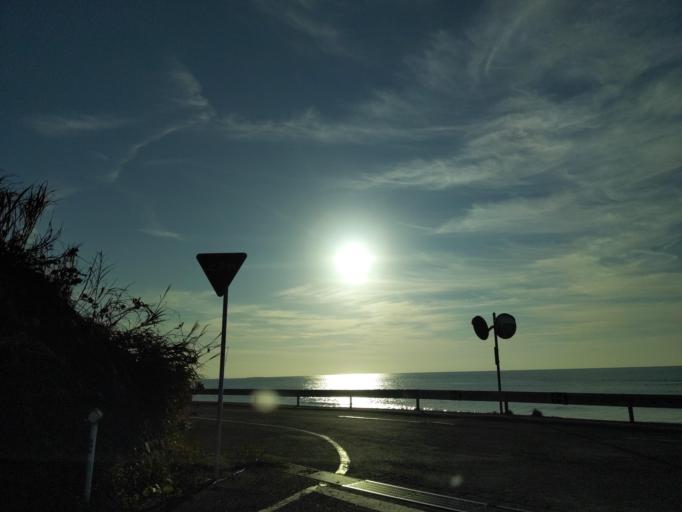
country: JP
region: Niigata
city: Nagaoka
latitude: 37.5759
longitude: 138.7259
